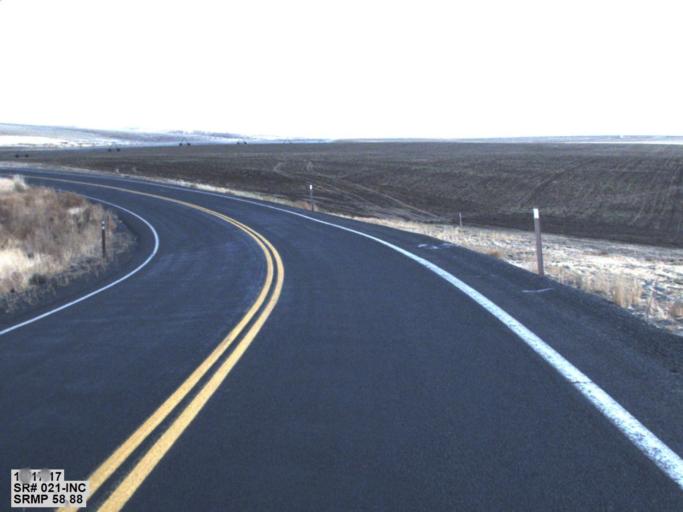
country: US
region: Washington
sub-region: Adams County
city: Ritzville
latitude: 47.3723
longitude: -118.6963
